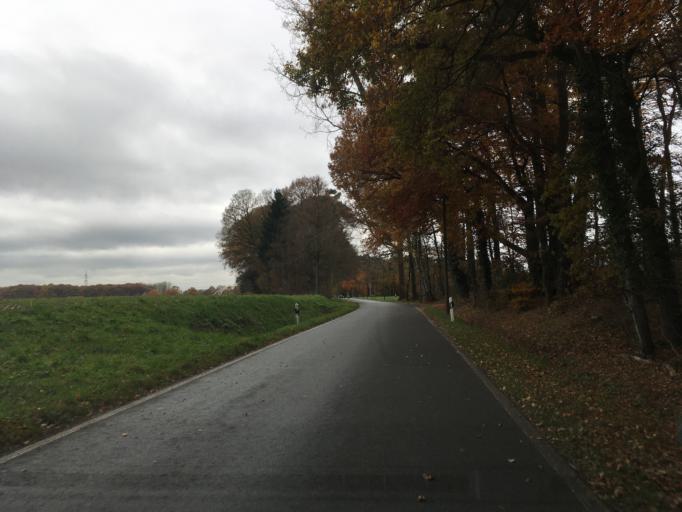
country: DE
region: North Rhine-Westphalia
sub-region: Regierungsbezirk Munster
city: Gescher
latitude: 51.9838
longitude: 6.9853
